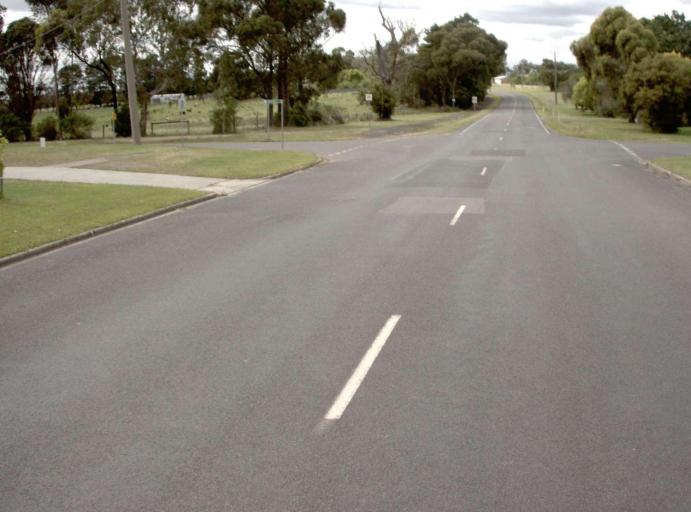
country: AU
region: Victoria
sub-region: Latrobe
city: Moe
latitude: -38.0738
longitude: 146.1797
